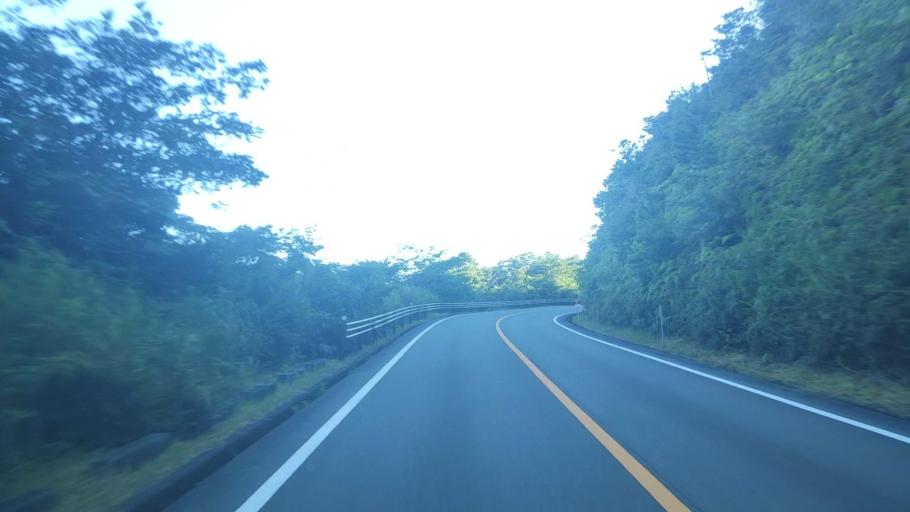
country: JP
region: Mie
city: Toba
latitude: 34.4113
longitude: 136.9023
